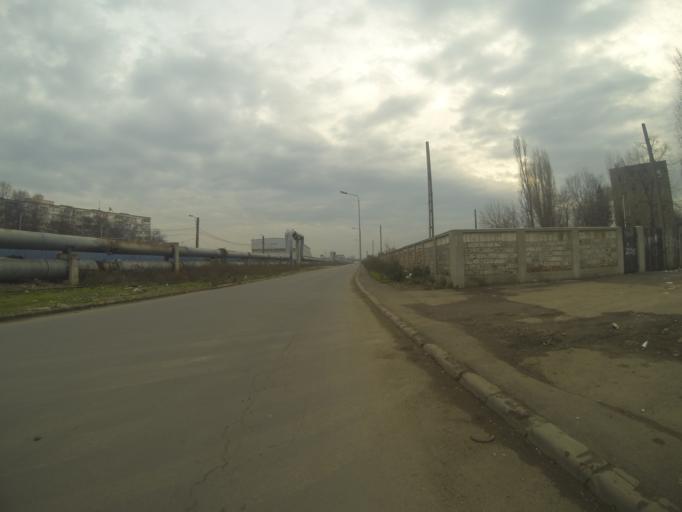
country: RO
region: Bucuresti
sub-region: Municipiul Bucuresti
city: Bucuresti
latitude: 44.3854
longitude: 26.0867
